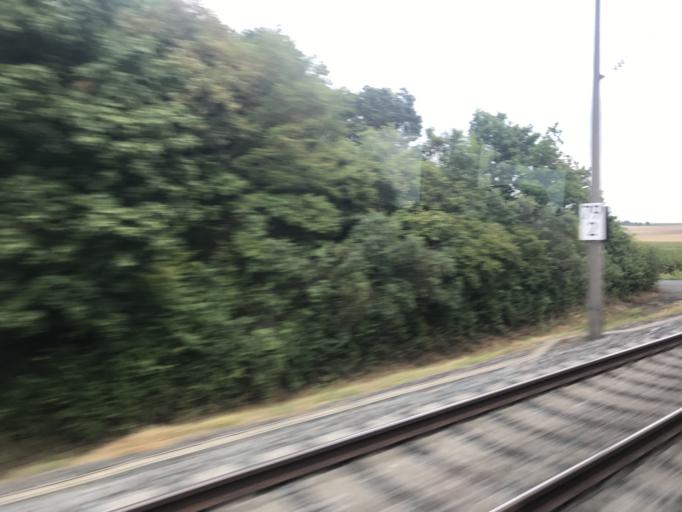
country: DE
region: Bavaria
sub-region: Regierungsbezirk Unterfranken
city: Oberpleichfeld
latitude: 49.8847
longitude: 10.0889
